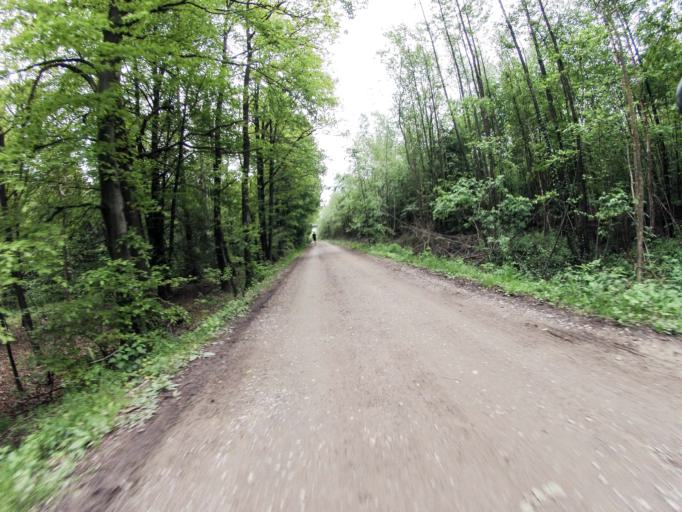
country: DE
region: Lower Saxony
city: Ostercappeln
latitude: 52.3404
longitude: 8.1804
